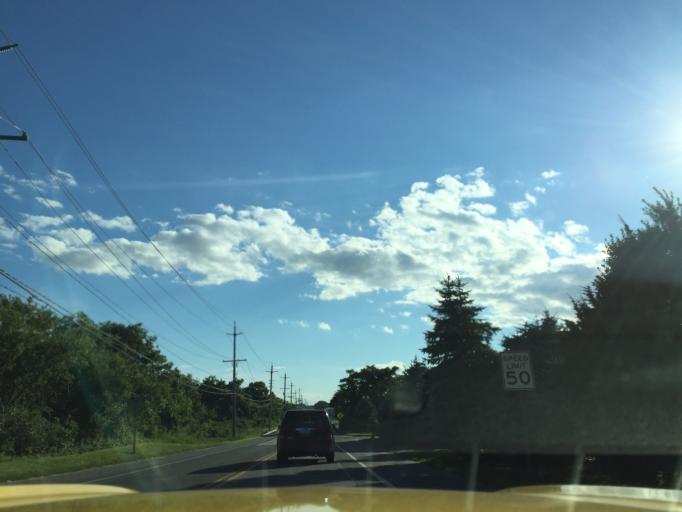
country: US
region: New York
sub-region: Suffolk County
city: Greenport West
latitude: 41.0982
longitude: -72.3917
